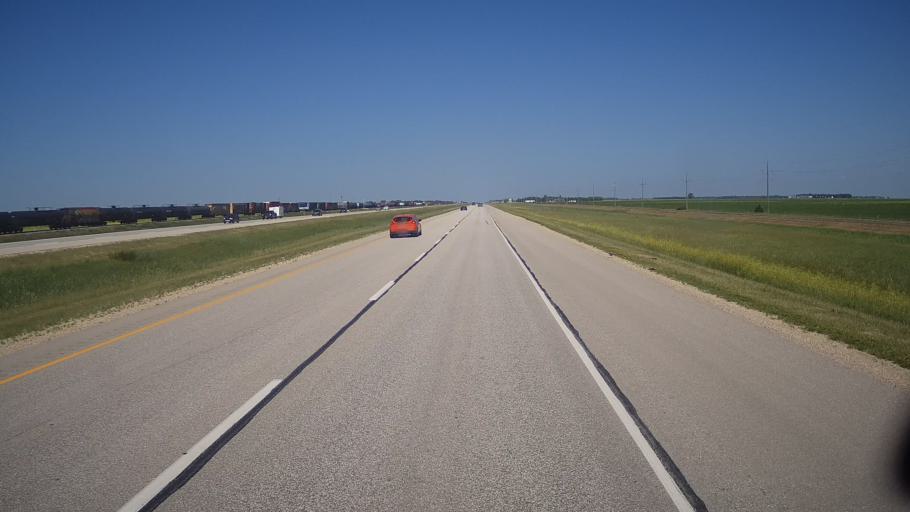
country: CA
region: Manitoba
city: Niverville
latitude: 49.7727
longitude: -96.8215
